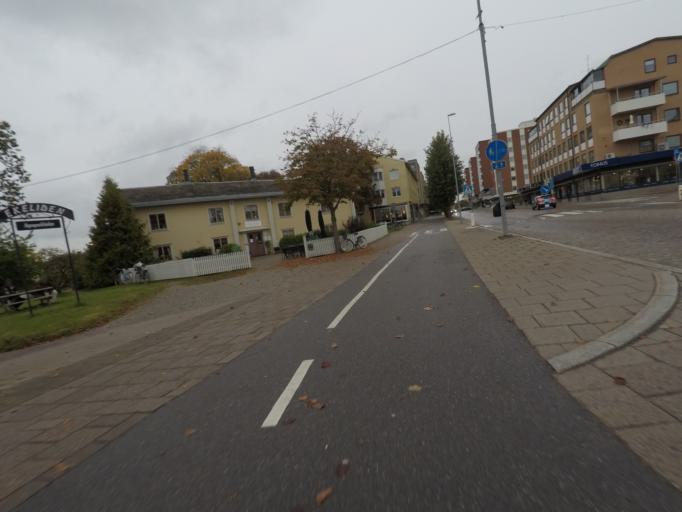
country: SE
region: OErebro
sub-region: Karlskoga Kommun
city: Karlskoga
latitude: 59.3253
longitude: 14.5171
